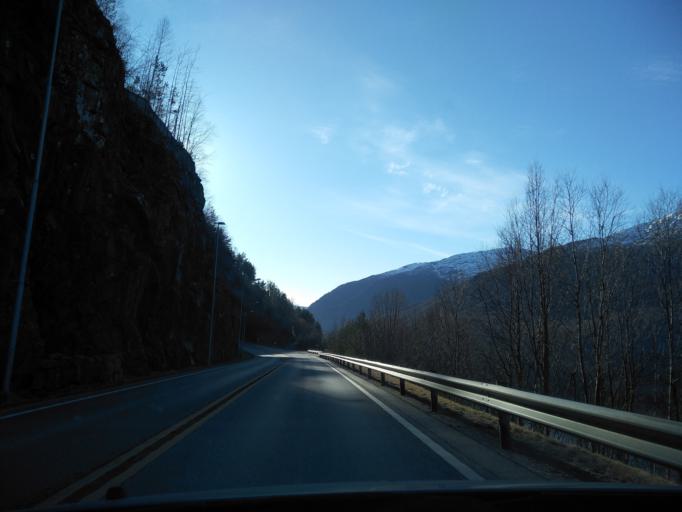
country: NO
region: Rogaland
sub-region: Sauda
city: Sauda
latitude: 59.8293
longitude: 6.2498
